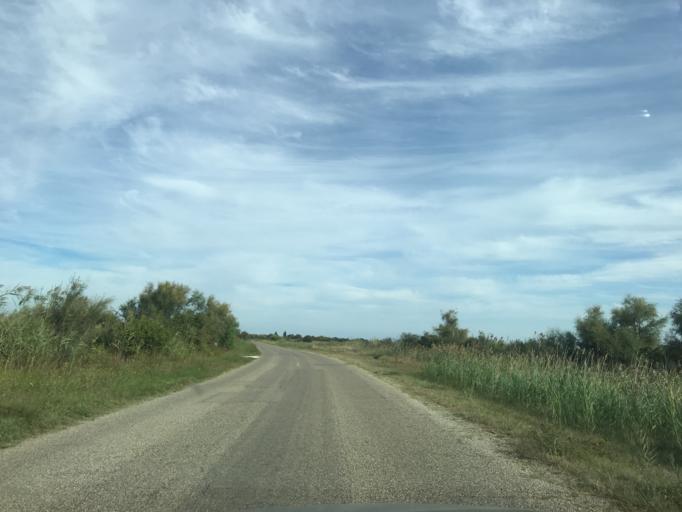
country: FR
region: Provence-Alpes-Cote d'Azur
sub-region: Departement des Bouches-du-Rhone
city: Saintes-Maries-de-la-Mer
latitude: 43.5220
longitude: 4.3866
